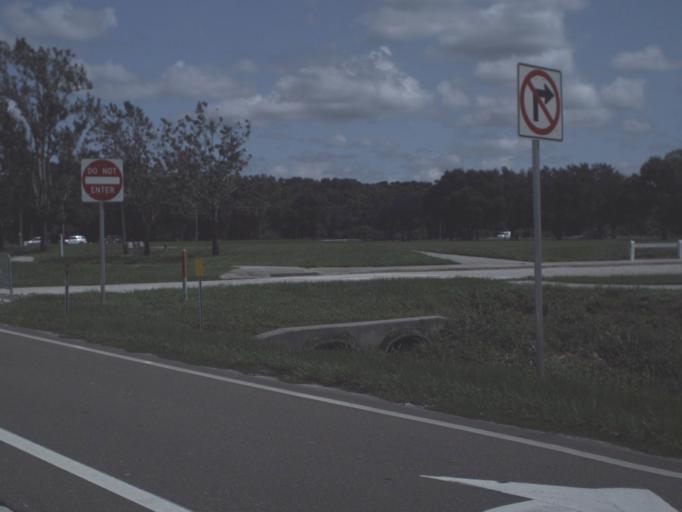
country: US
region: Florida
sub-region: Hillsborough County
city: Egypt Lake-Leto
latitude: 27.9801
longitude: -82.5053
